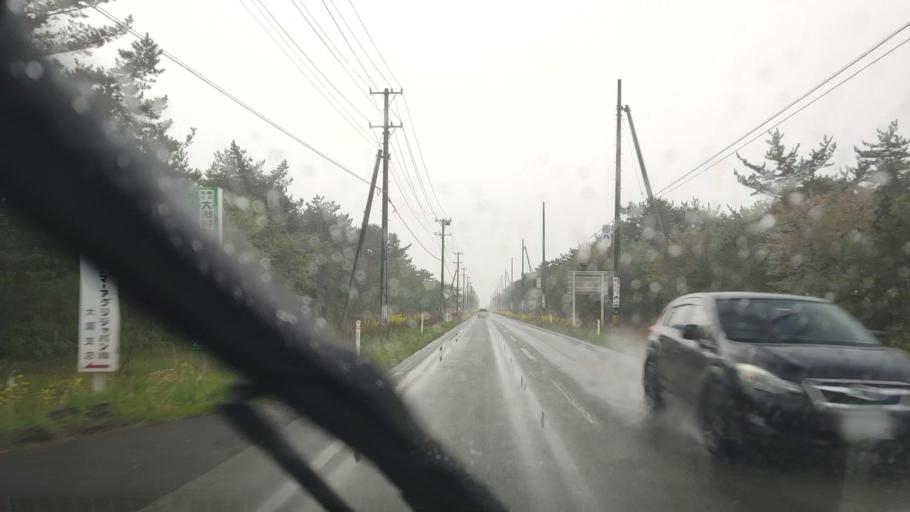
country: JP
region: Akita
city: Tenno
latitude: 40.0075
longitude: 139.9502
